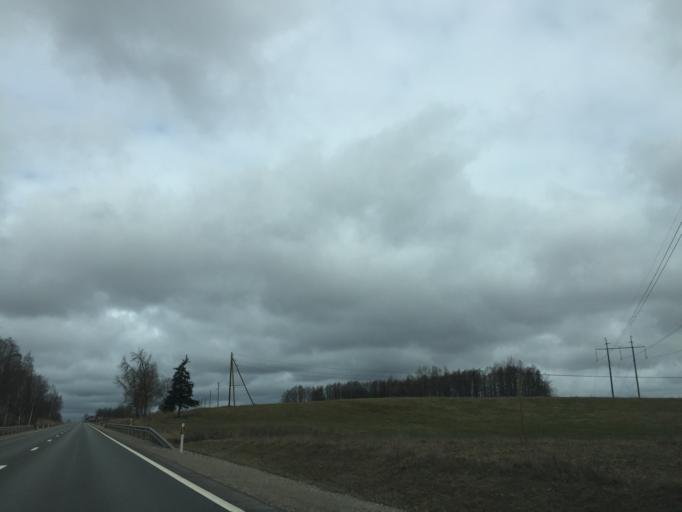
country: LV
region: Daugavpils
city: Daugavpils
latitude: 55.8881
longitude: 26.4037
